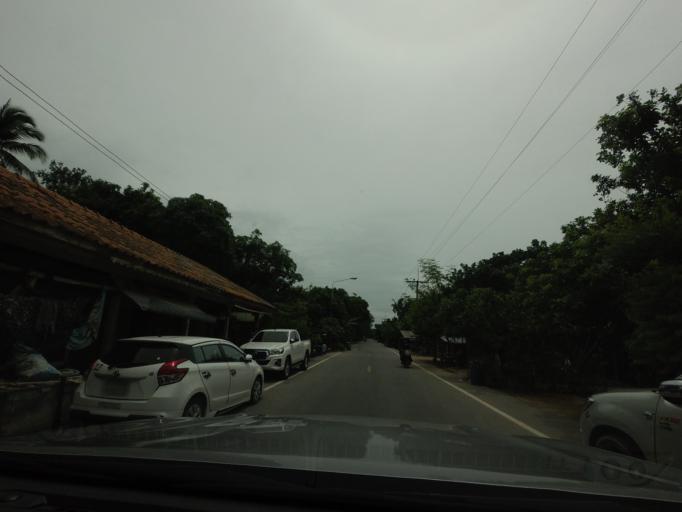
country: TH
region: Pattani
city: Kapho
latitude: 6.6201
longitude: 101.5433
